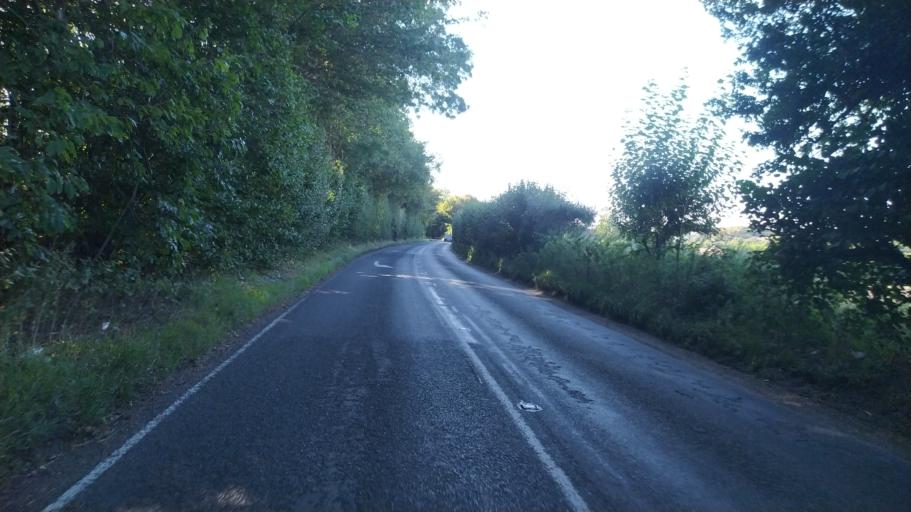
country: GB
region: England
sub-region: Hampshire
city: Alton
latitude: 51.1417
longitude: -0.9482
